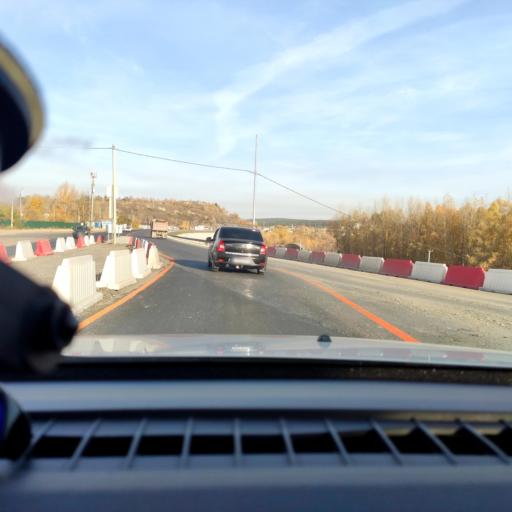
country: RU
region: Samara
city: Volzhskiy
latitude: 53.4151
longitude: 50.1323
